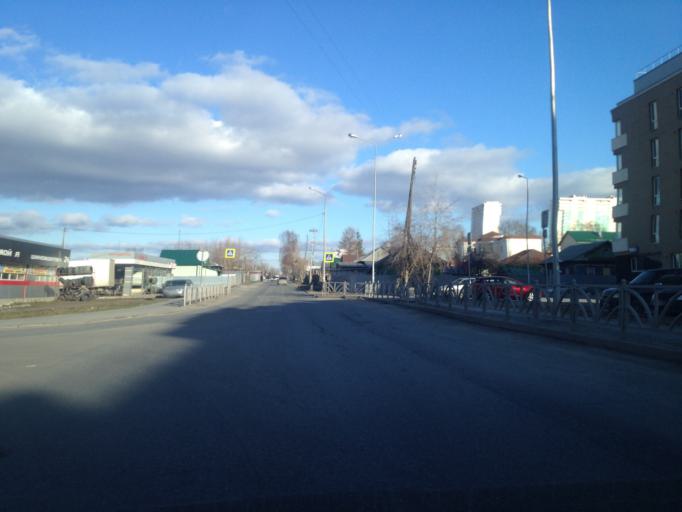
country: RU
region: Sverdlovsk
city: Sovkhoznyy
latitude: 56.8052
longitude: 60.5768
